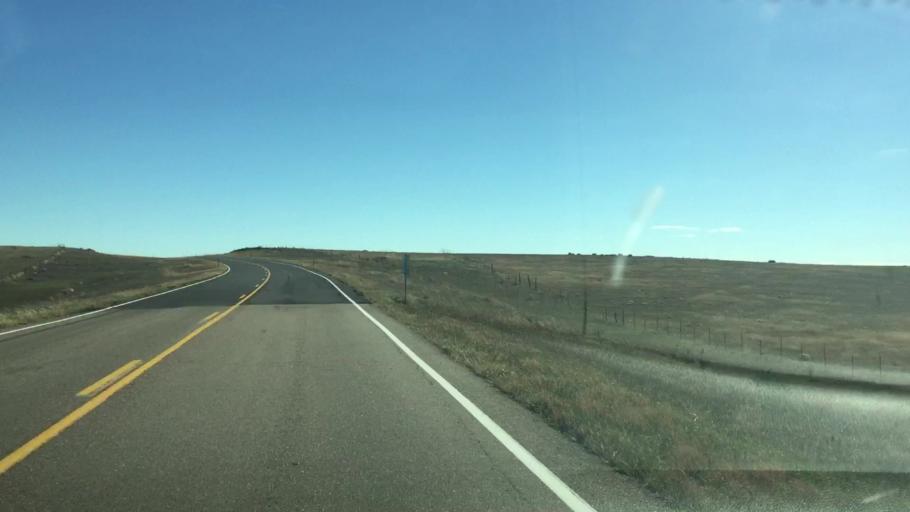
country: US
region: Colorado
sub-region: Lincoln County
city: Limon
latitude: 39.2958
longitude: -103.8597
